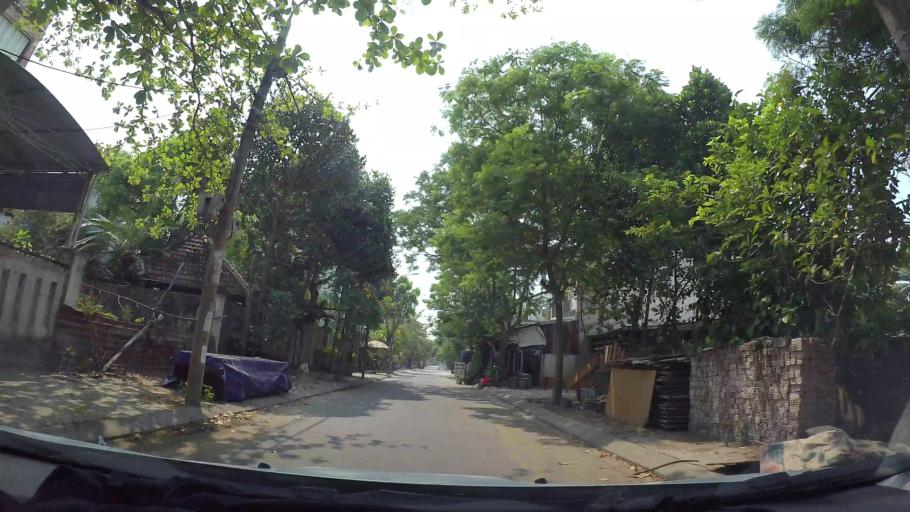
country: VN
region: Da Nang
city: Cam Le
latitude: 15.9991
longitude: 108.2060
